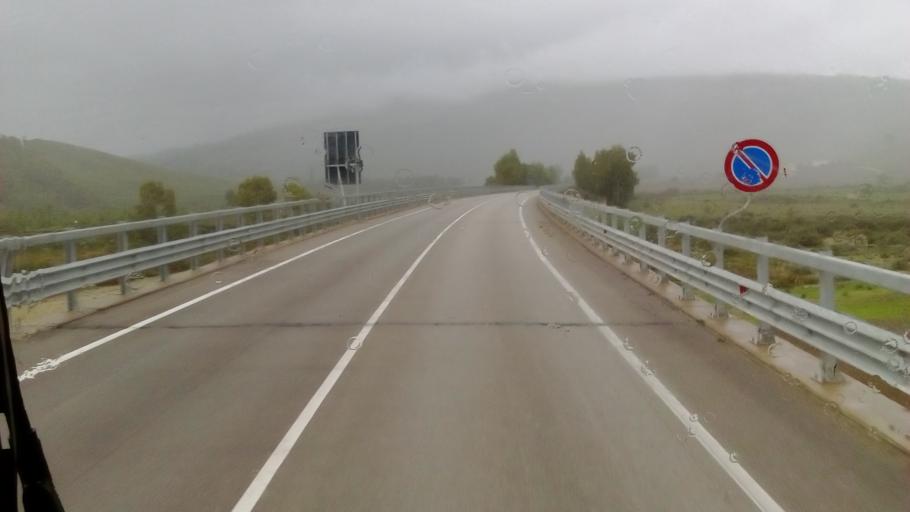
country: IT
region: Sicily
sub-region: Enna
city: Villarosa
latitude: 37.5321
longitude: 14.1298
